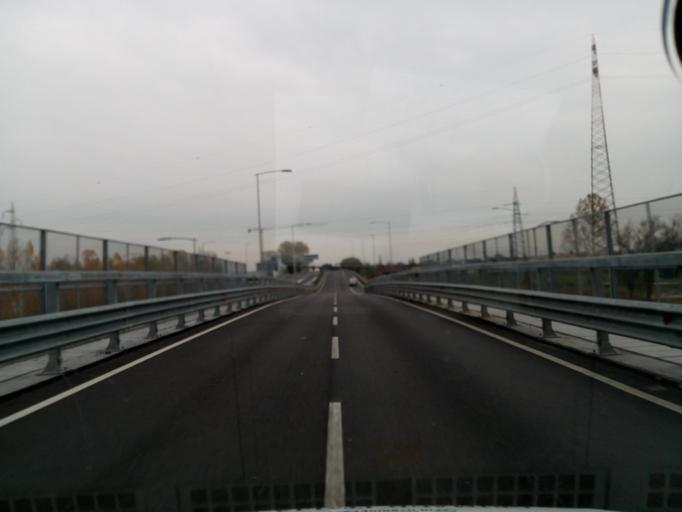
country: IT
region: Veneto
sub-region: Provincia di Padova
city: Villatora
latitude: 45.3892
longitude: 11.9539
